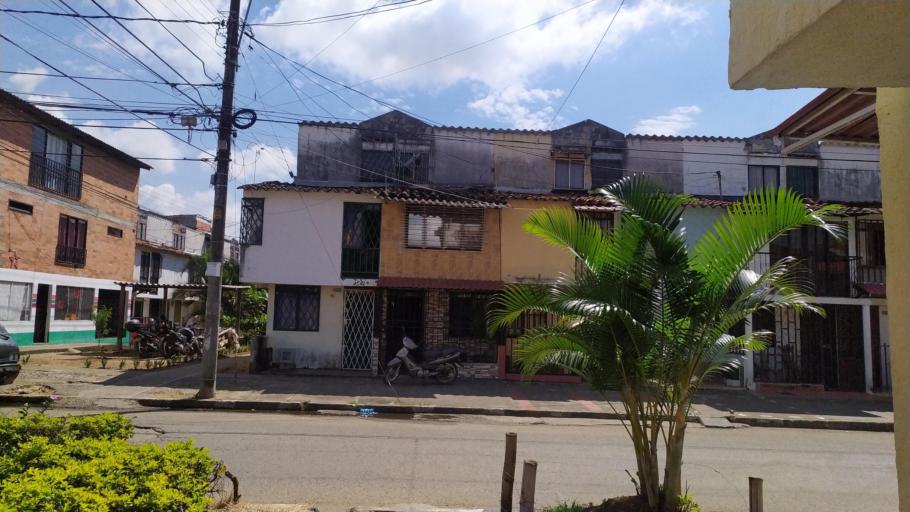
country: CO
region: Valle del Cauca
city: Jamundi
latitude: 3.2544
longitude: -76.5453
